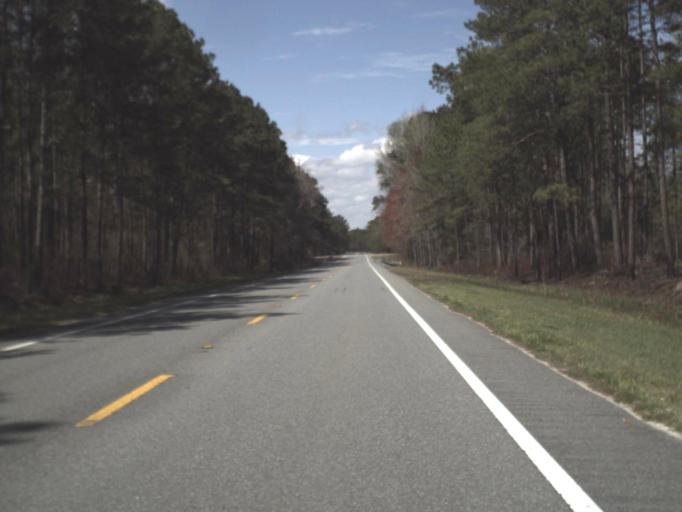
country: US
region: Florida
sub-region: Gadsden County
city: Midway
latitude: 30.3826
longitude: -84.5669
